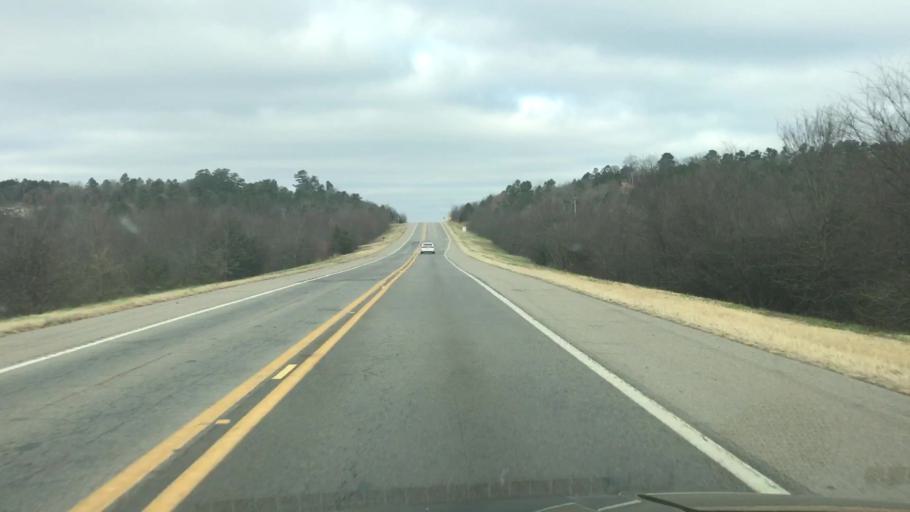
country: US
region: Arkansas
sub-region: Scott County
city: Waldron
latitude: 34.8584
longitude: -94.0689
